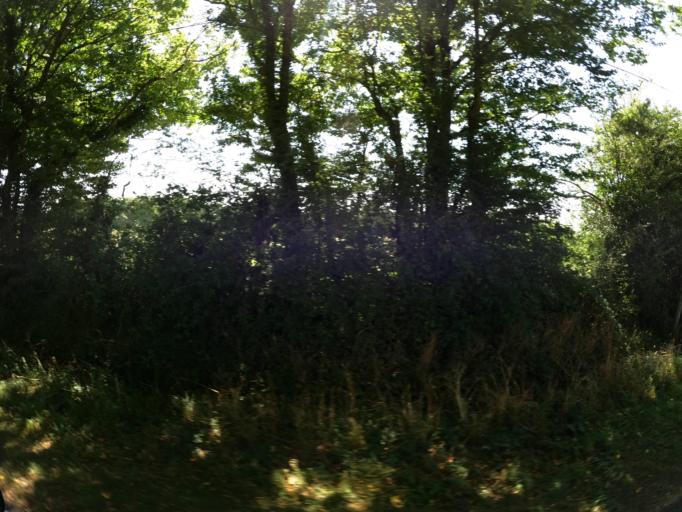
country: FR
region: Poitou-Charentes
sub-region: Departement de la Vienne
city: Charroux
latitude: 46.1406
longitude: 0.4257
